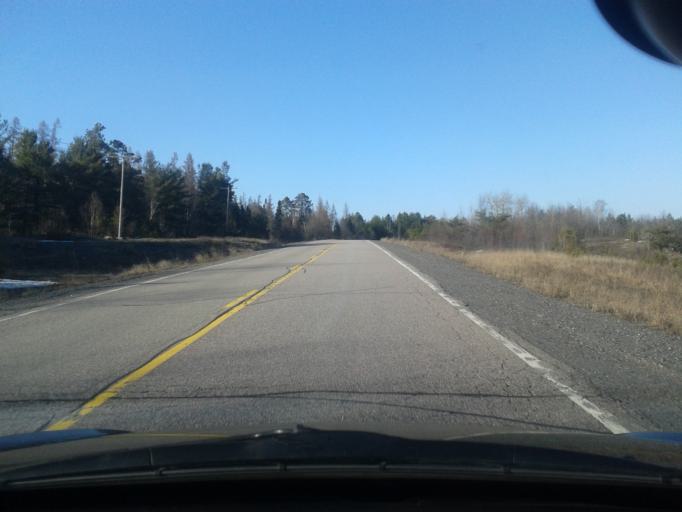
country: CA
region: Ontario
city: Greater Sudbury
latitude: 46.2618
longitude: -80.3050
